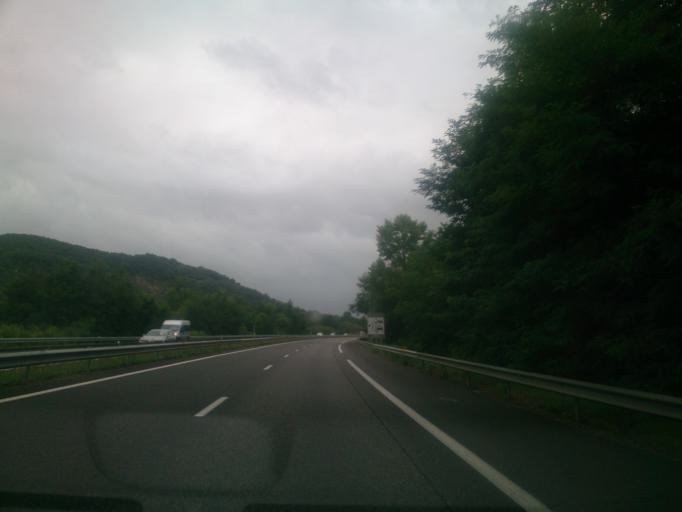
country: FR
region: Midi-Pyrenees
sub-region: Departement de la Haute-Garonne
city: Martres-Tolosane
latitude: 43.1782
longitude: 0.9786
